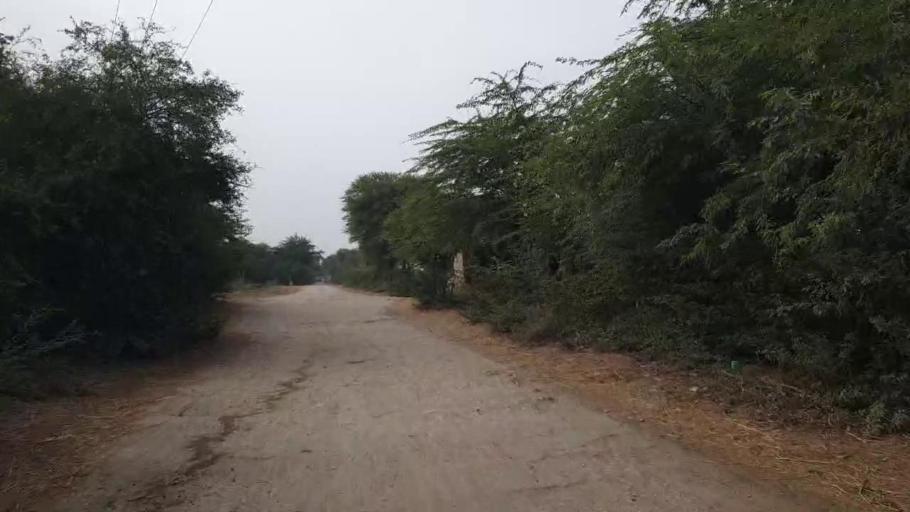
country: PK
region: Sindh
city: Matli
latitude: 24.9513
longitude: 68.5809
